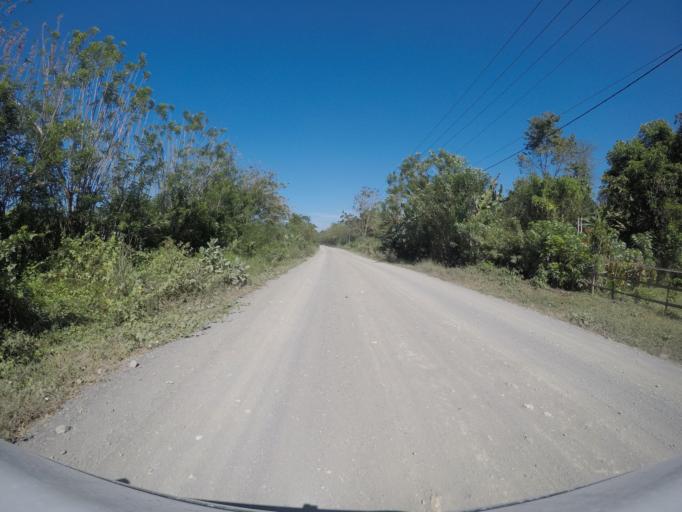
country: TL
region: Viqueque
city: Viqueque
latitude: -8.9728
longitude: 126.0697
